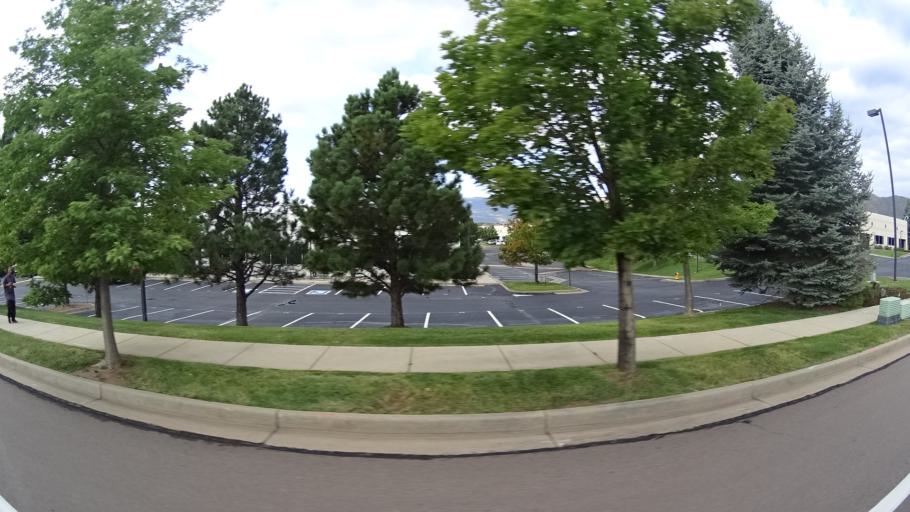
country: US
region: Colorado
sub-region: El Paso County
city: Colorado Springs
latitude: 38.9014
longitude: -104.8544
